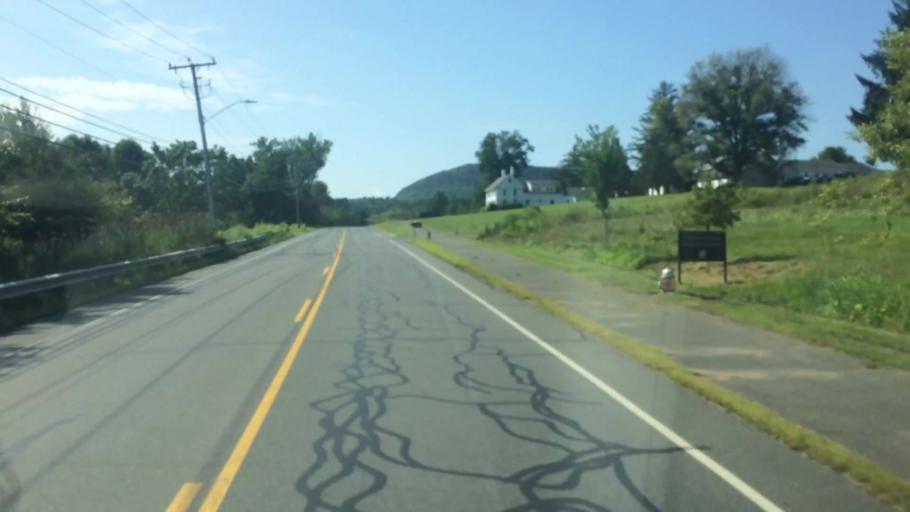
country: US
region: Massachusetts
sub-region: Hampshire County
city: South Amherst
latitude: 42.3279
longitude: -72.5243
